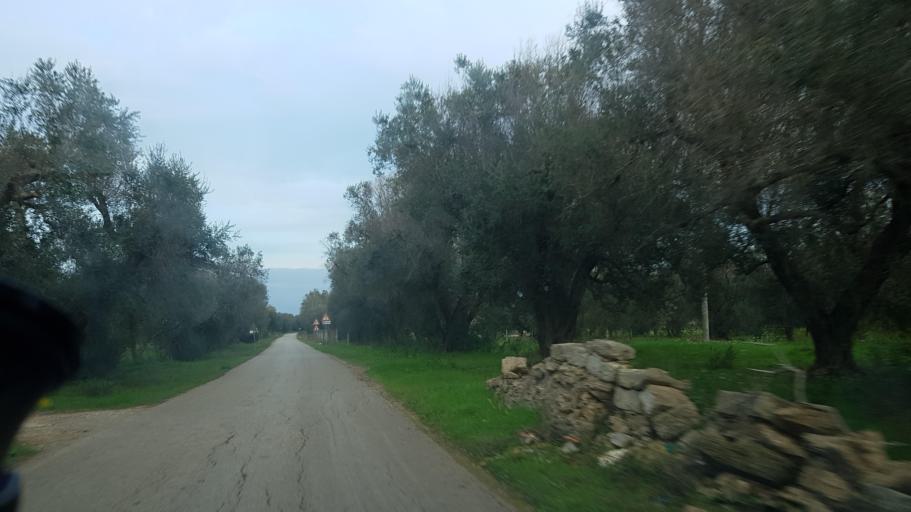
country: IT
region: Apulia
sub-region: Provincia di Brindisi
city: Latiano
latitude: 40.5376
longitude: 17.7575
